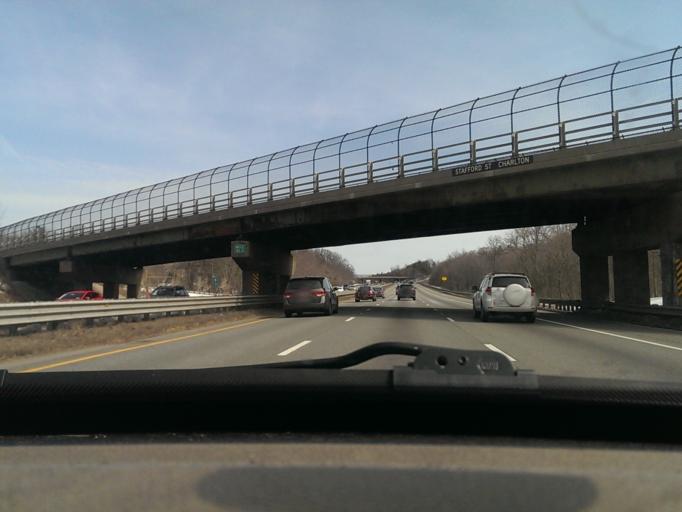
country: US
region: Massachusetts
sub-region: Worcester County
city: Charlton
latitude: 42.1530
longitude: -71.9791
